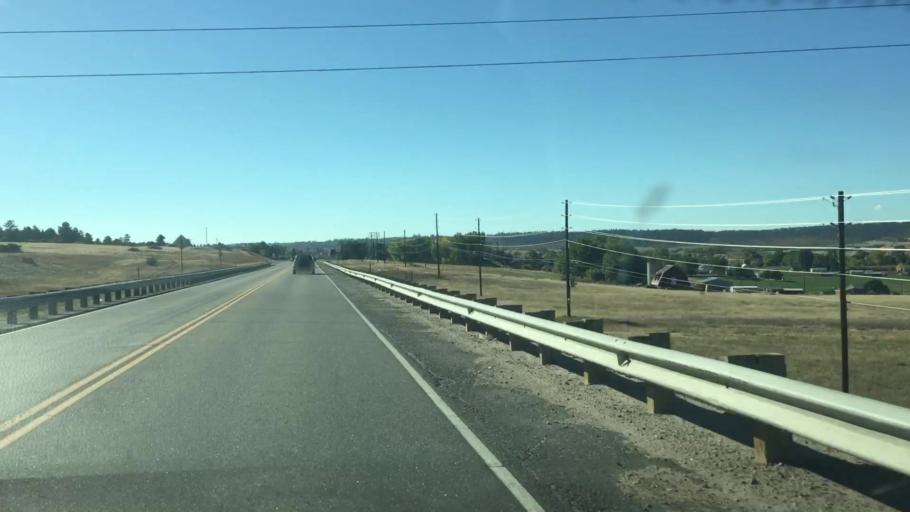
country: US
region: Colorado
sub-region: Douglas County
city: The Pinery
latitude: 39.3989
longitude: -104.7560
